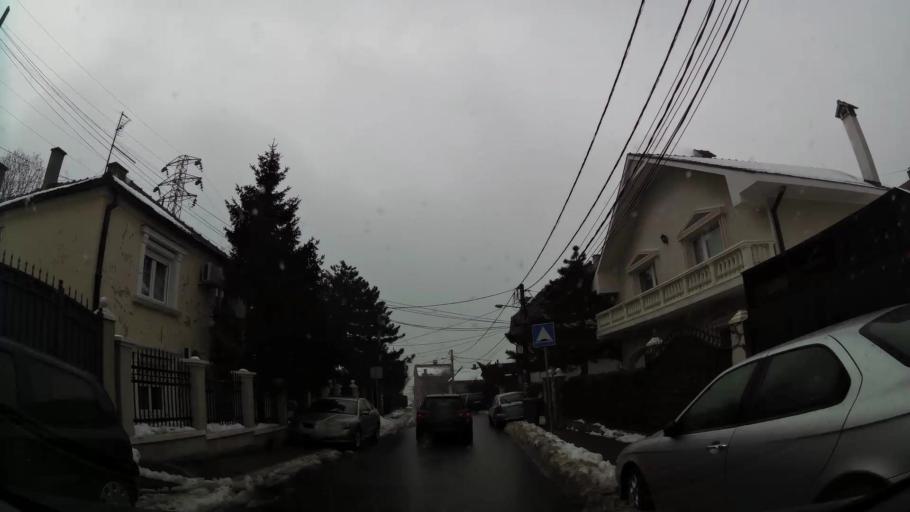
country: RS
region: Central Serbia
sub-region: Belgrade
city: Zvezdara
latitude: 44.7806
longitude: 20.5194
